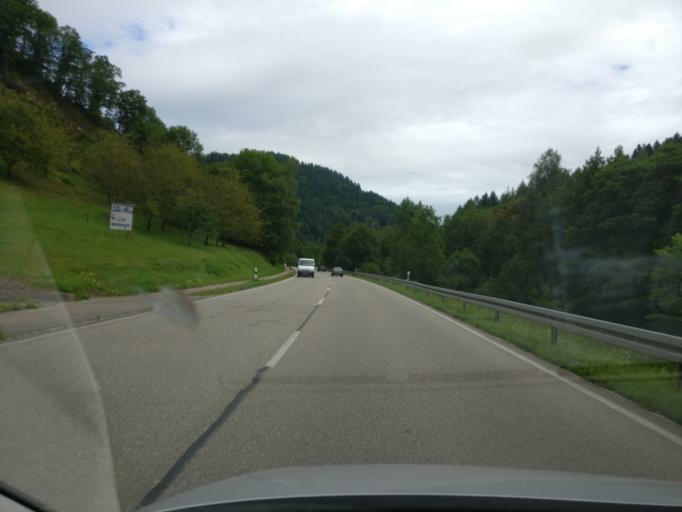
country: DE
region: Baden-Wuerttemberg
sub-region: Freiburg Region
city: Lautenbach
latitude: 48.5118
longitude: 8.1293
